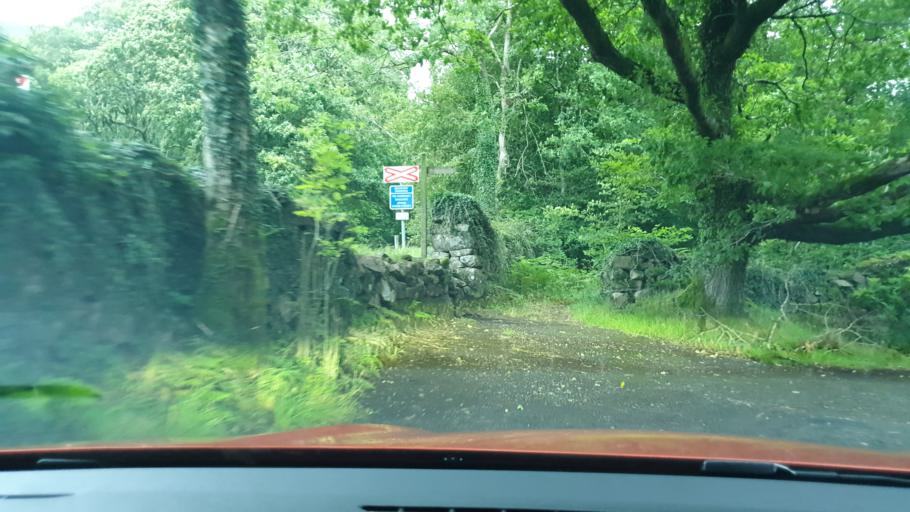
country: GB
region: England
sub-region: Cumbria
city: Millom
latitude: 54.3927
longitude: -3.2821
